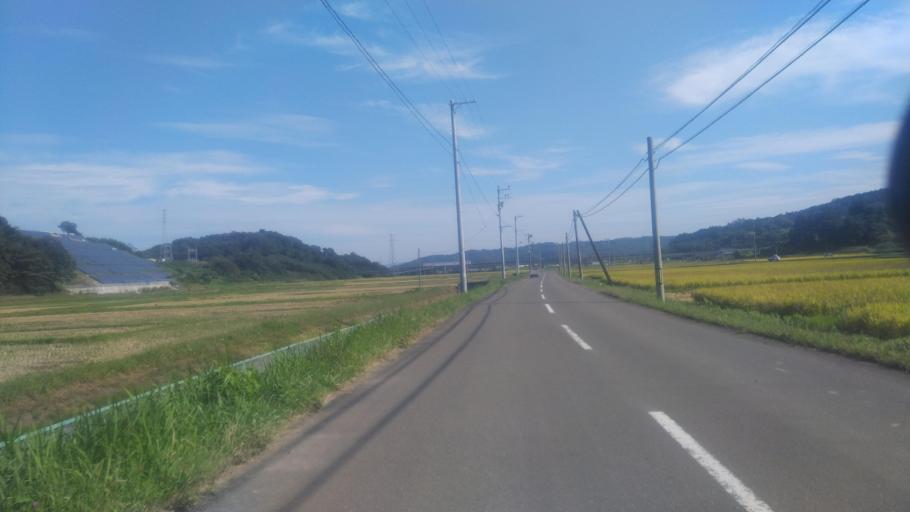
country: JP
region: Miyagi
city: Okawara
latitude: 38.0554
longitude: 140.6939
